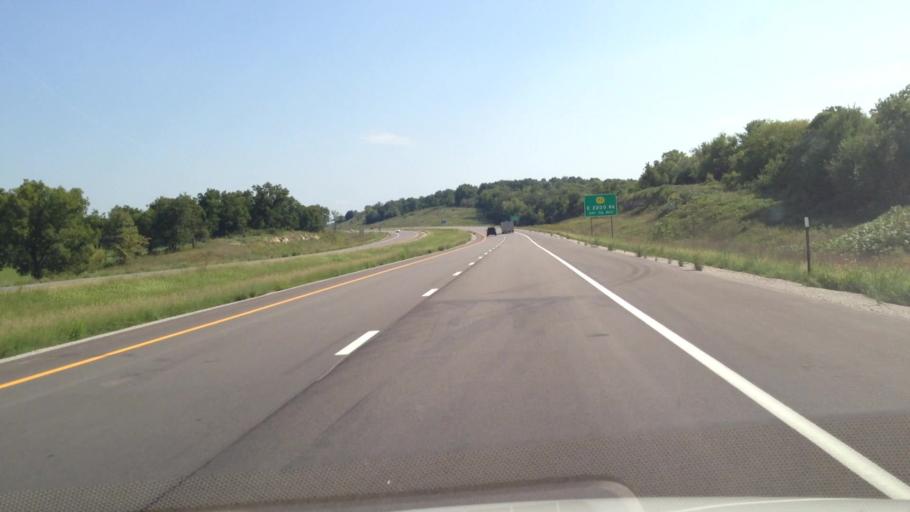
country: US
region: Kansas
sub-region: Linn County
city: La Cygne
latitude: 38.3591
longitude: -94.6876
